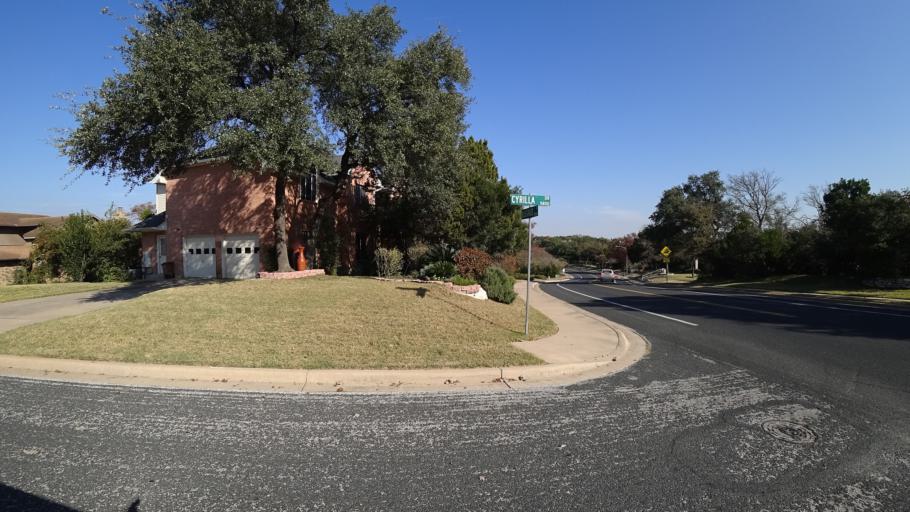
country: US
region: Texas
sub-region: Williamson County
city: Jollyville
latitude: 30.3930
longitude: -97.7699
